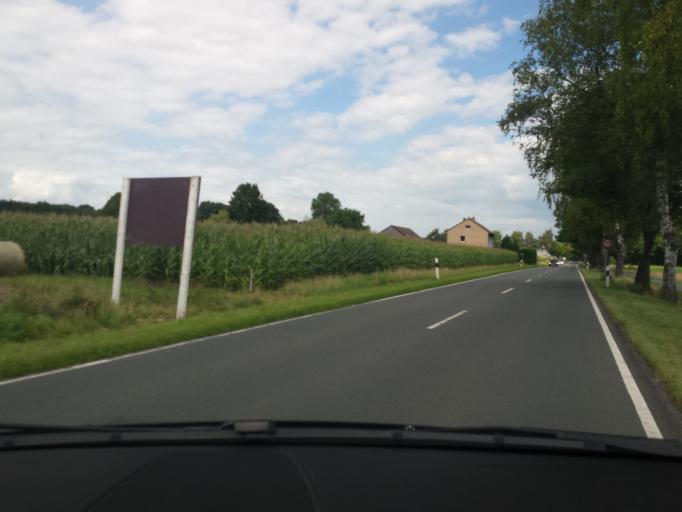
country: DE
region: North Rhine-Westphalia
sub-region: Regierungsbezirk Arnsberg
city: Lippstadt
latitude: 51.6950
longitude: 8.3102
